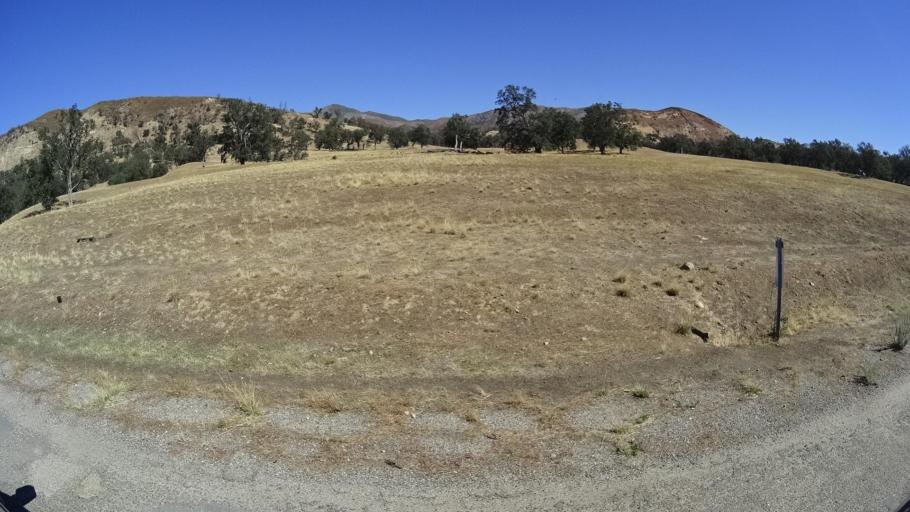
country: US
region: California
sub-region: Monterey County
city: Greenfield
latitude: 36.0855
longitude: -121.4034
